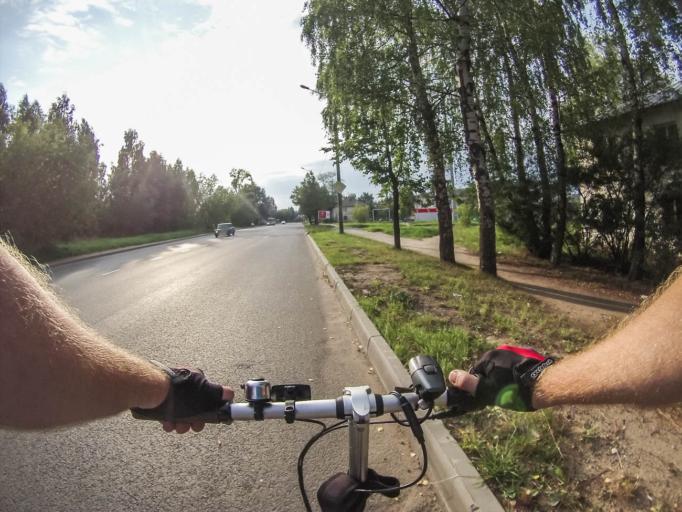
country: RU
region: Kostroma
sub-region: Kostromskoy Rayon
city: Kostroma
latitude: 57.7831
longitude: 40.8775
